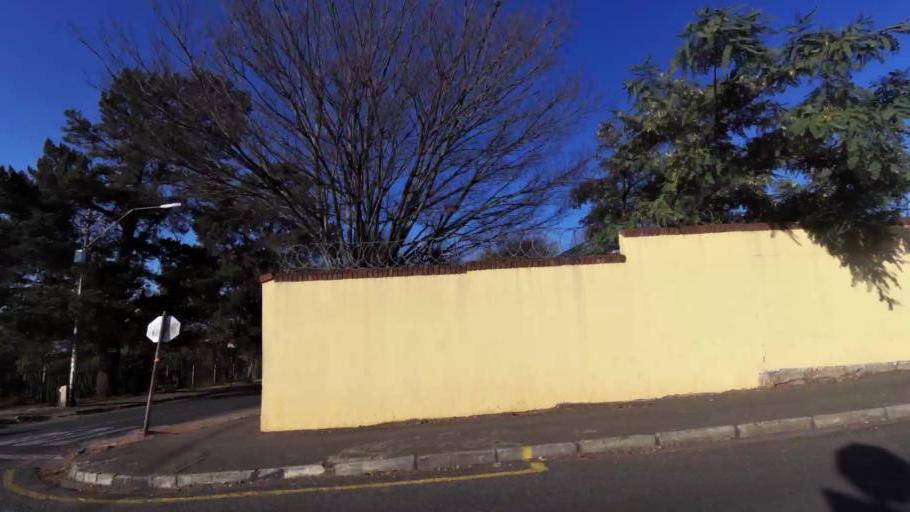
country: ZA
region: Gauteng
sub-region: City of Johannesburg Metropolitan Municipality
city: Johannesburg
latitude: -26.1891
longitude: 27.9932
